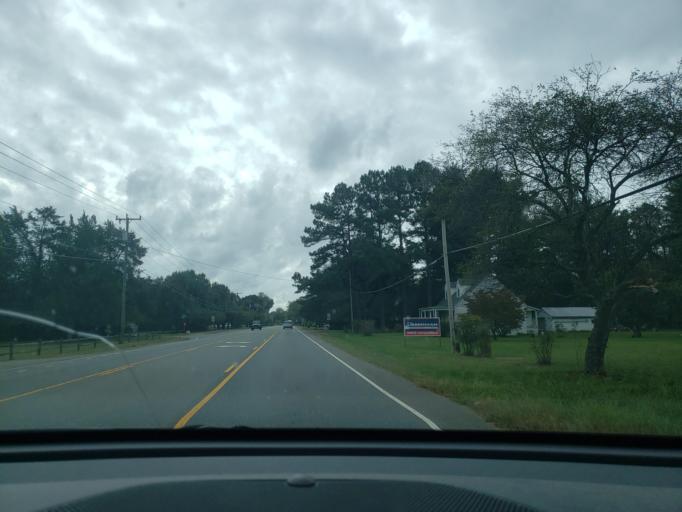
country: US
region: Virginia
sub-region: City of Fredericksburg
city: Fredericksburg
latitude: 38.2502
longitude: -77.4241
